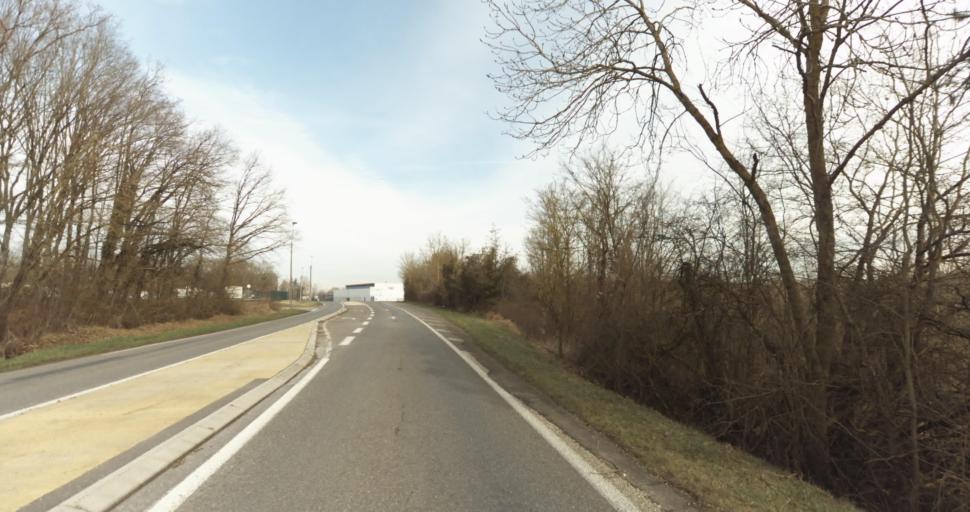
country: FR
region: Lorraine
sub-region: Departement de Meurthe-et-Moselle
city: Jarny
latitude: 49.1357
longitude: 5.8928
